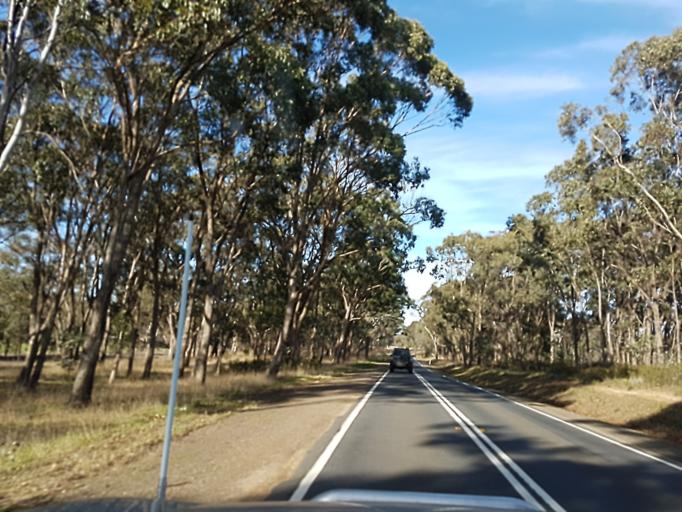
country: AU
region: Victoria
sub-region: Murrindindi
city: Alexandra
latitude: -37.1478
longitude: 145.6407
